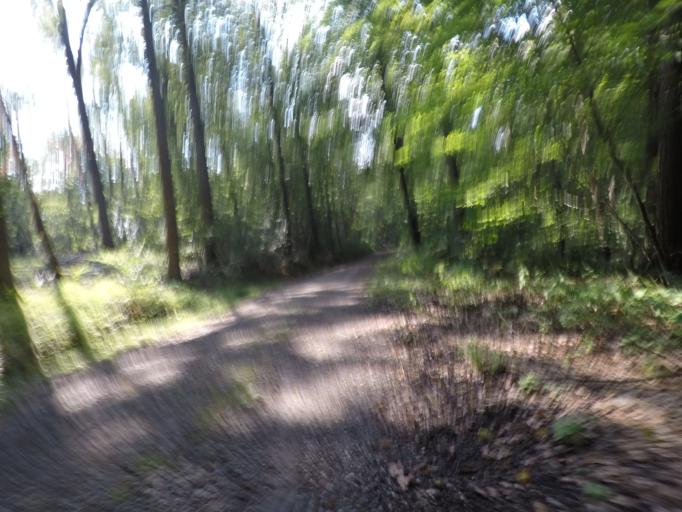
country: DE
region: Baden-Wuerttemberg
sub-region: Regierungsbezirk Stuttgart
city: Steinenbronn
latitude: 48.6550
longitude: 9.1093
